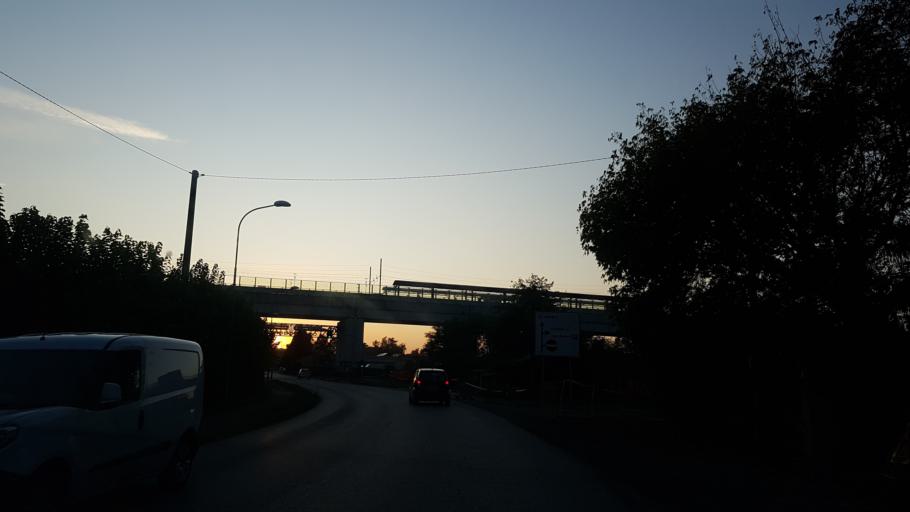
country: IT
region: Emilia-Romagna
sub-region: Provincia di Modena
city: Camposanto
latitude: 44.7880
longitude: 11.1451
